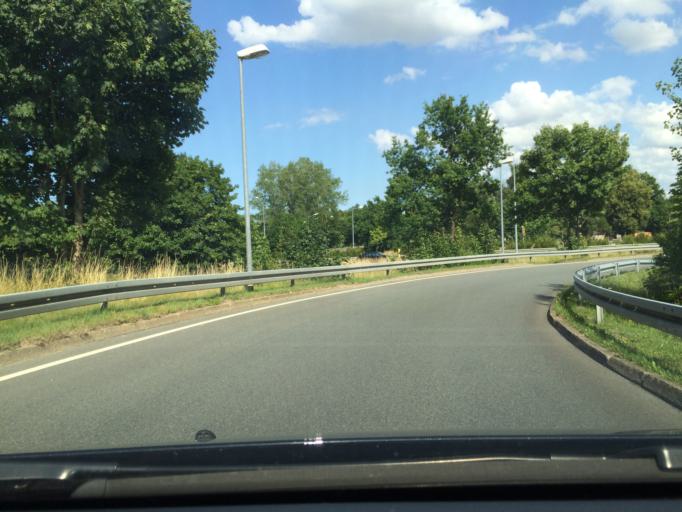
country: DE
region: Mecklenburg-Vorpommern
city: Warnemuende
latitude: 54.1395
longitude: 12.0613
